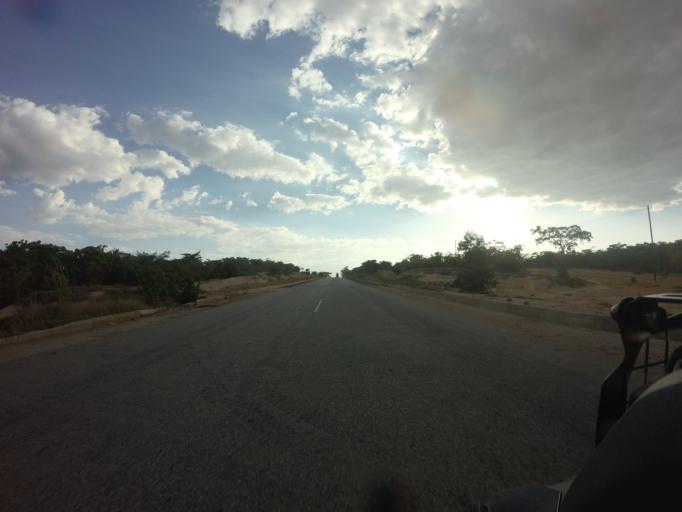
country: AO
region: Huila
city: Lubango
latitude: -14.7320
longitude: 13.8796
